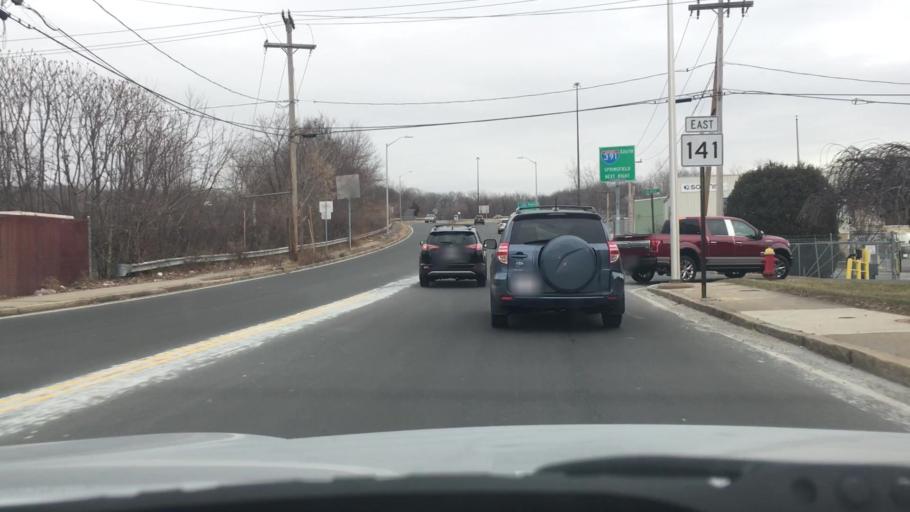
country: US
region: Massachusetts
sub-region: Hampden County
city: North Chicopee
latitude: 42.1827
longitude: -72.6104
